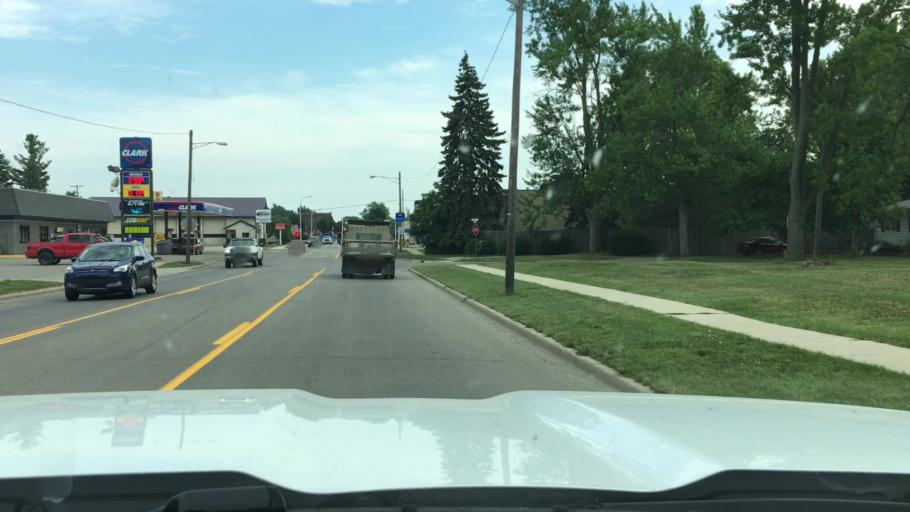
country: US
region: Michigan
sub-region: Sanilac County
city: Marlette
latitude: 43.3308
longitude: -83.0800
